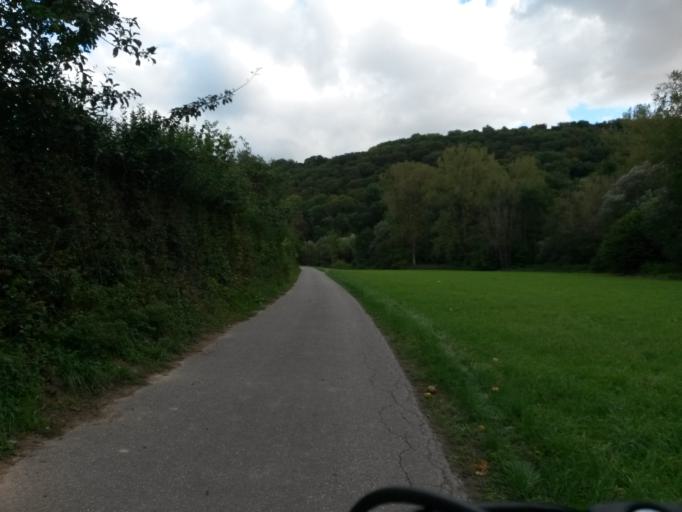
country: DE
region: Baden-Wuerttemberg
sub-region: Regierungsbezirk Stuttgart
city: Markgroningen
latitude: 48.9288
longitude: 9.0769
